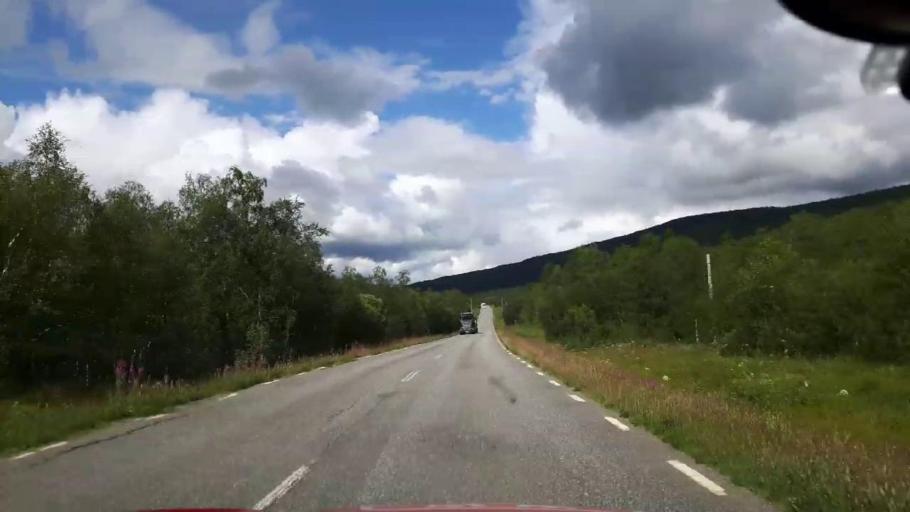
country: NO
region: Nordland
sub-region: Hattfjelldal
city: Hattfjelldal
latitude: 65.0551
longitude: 14.7289
